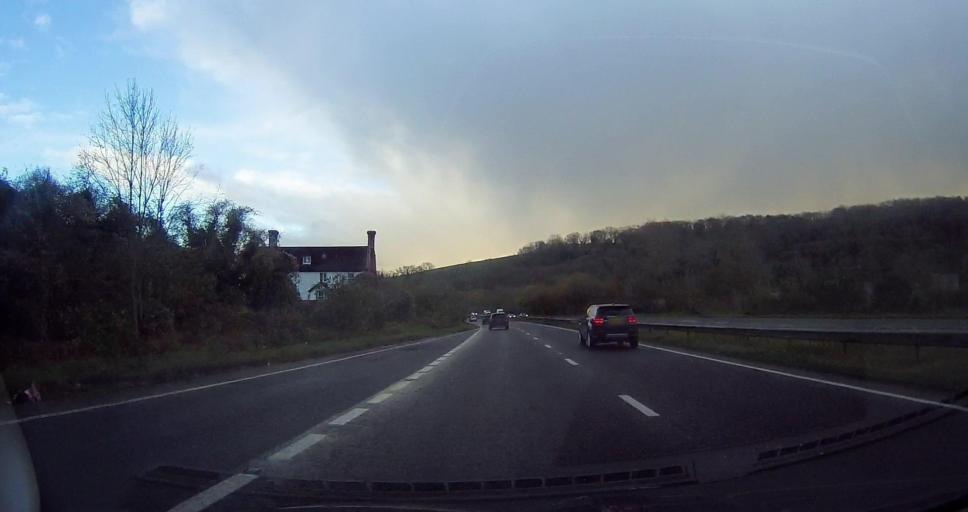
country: GB
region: England
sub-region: West Sussex
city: Hurstpierpoint
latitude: 50.9052
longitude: -0.1856
